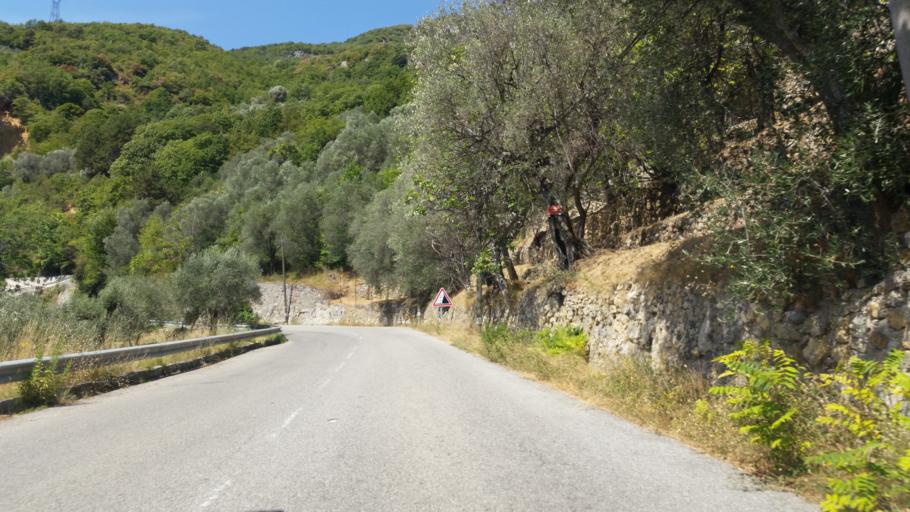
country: FR
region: Provence-Alpes-Cote d'Azur
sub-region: Departement des Alpes-Maritimes
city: Breil-sur-Roya
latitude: 43.9492
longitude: 7.5145
